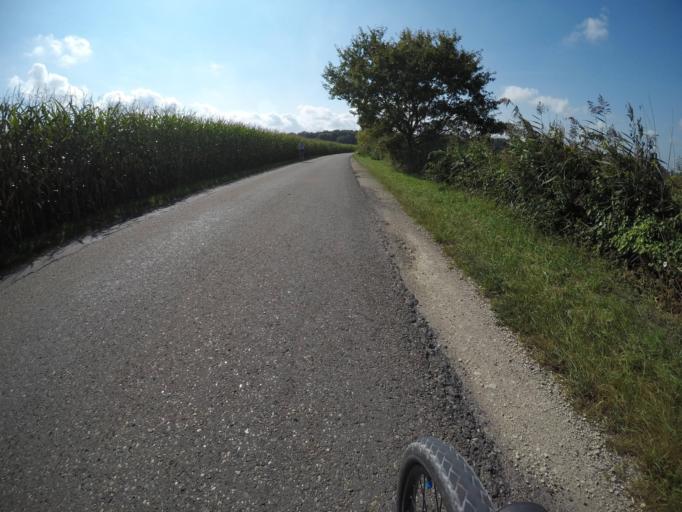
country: DE
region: Bavaria
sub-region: Swabia
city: Tapfheim
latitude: 48.6540
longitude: 10.7185
